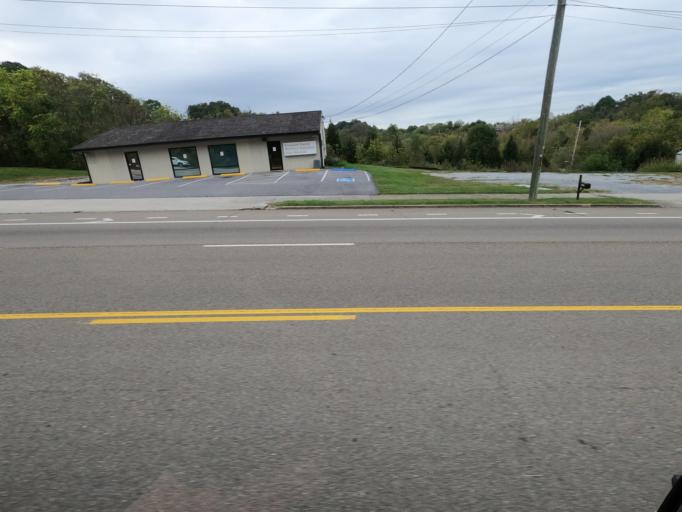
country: US
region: Virginia
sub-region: Scott County
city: Weber City
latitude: 36.5887
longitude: -82.5709
